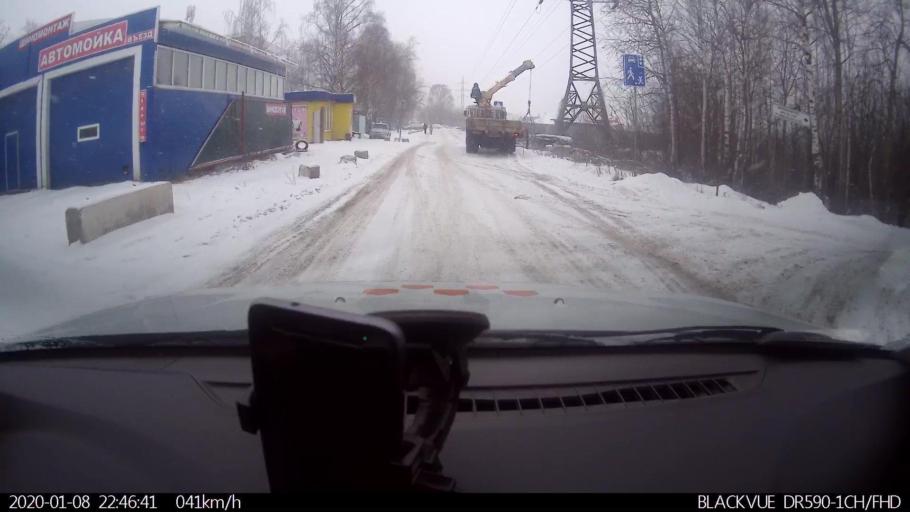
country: RU
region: Nizjnij Novgorod
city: Nizhniy Novgorod
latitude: 56.2945
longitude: 43.8933
